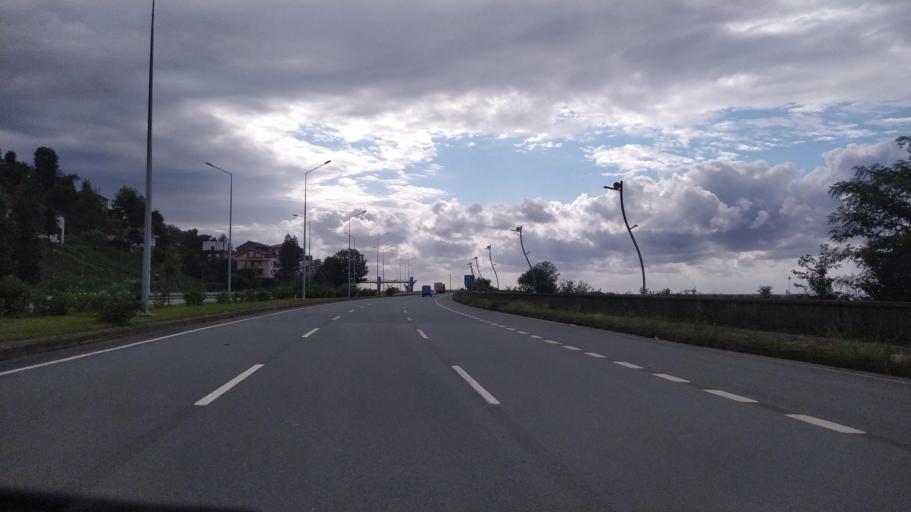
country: TR
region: Rize
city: Ardesen
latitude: 41.2103
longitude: 41.0405
